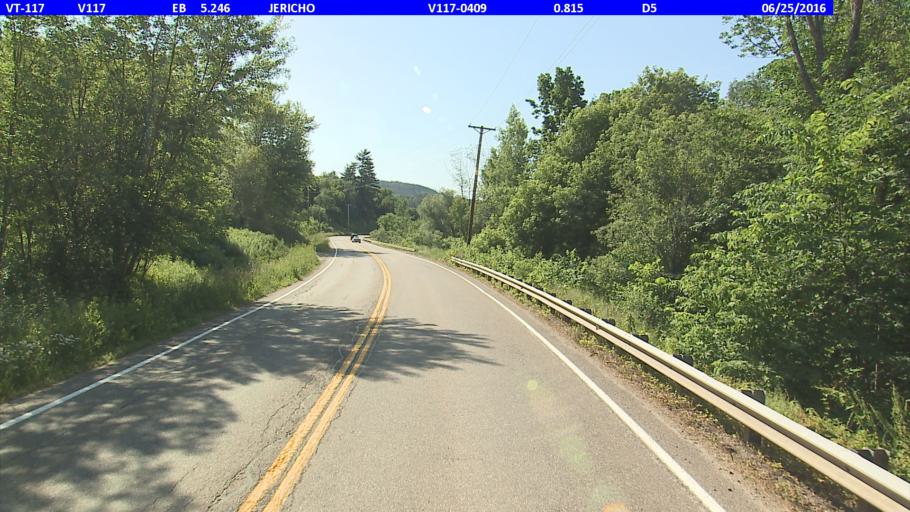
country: US
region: Vermont
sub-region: Chittenden County
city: Jericho
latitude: 44.4618
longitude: -73.0231
